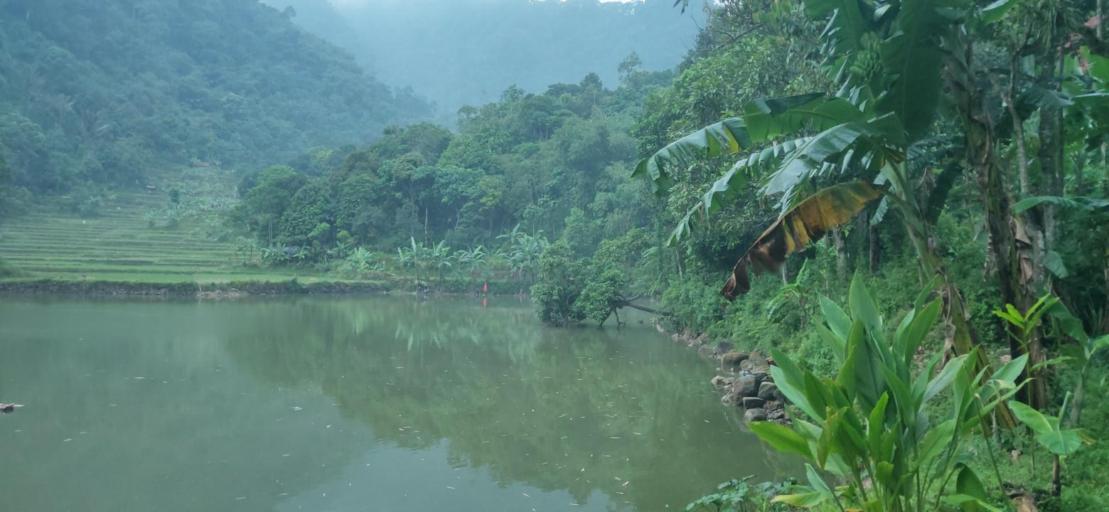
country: ID
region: West Java
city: Sidoger Lebak
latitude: -6.6089
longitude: 106.5556
